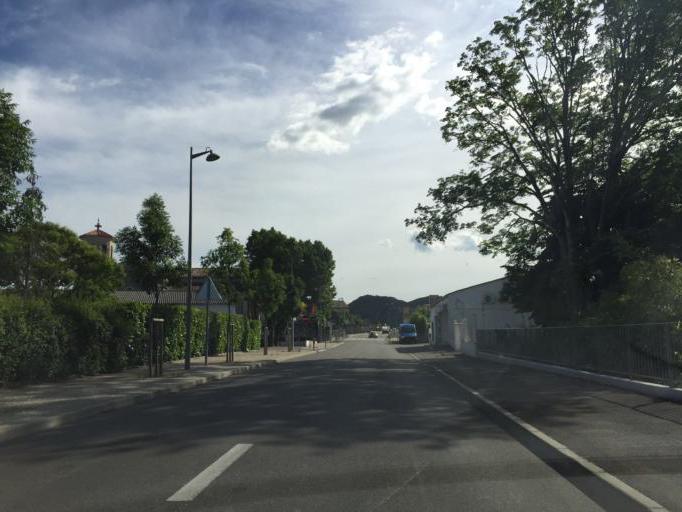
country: FR
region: Rhone-Alpes
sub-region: Departement de l'Ardeche
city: Meysse
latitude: 44.6094
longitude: 4.7247
